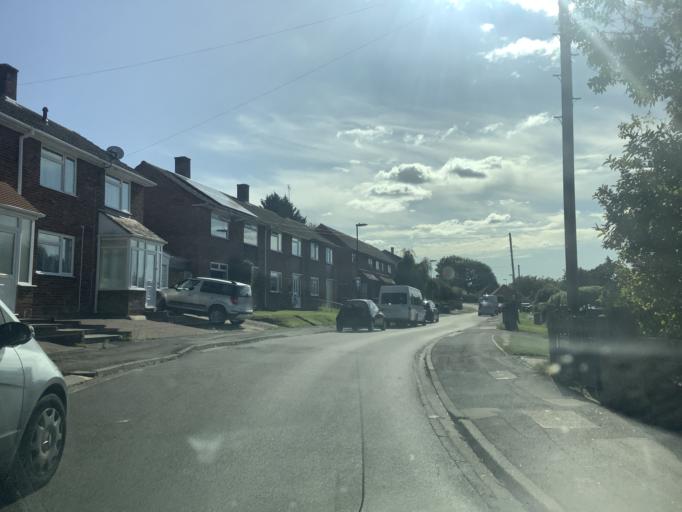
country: GB
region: England
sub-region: Hampshire
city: Marchwood
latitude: 50.9324
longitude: -1.4435
